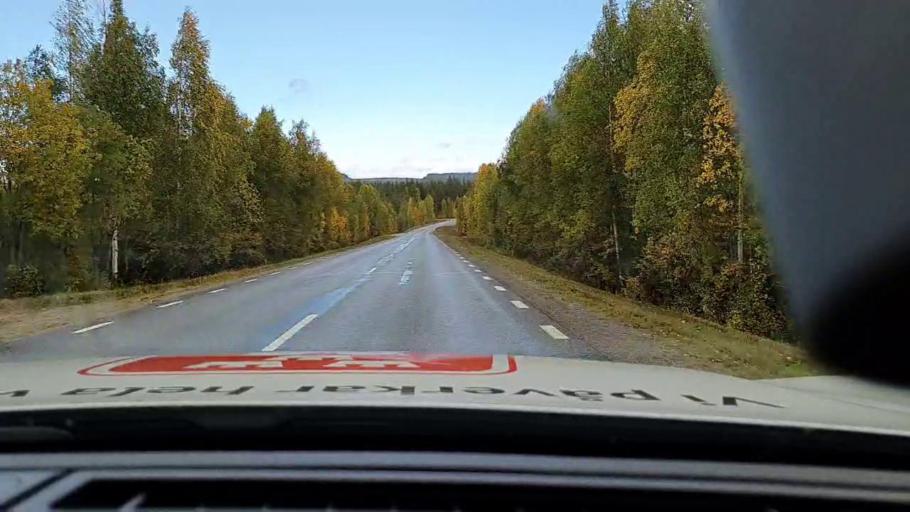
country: SE
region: Vaesterbotten
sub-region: Norsjo Kommun
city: Norsjoe
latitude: 64.9600
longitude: 19.6945
